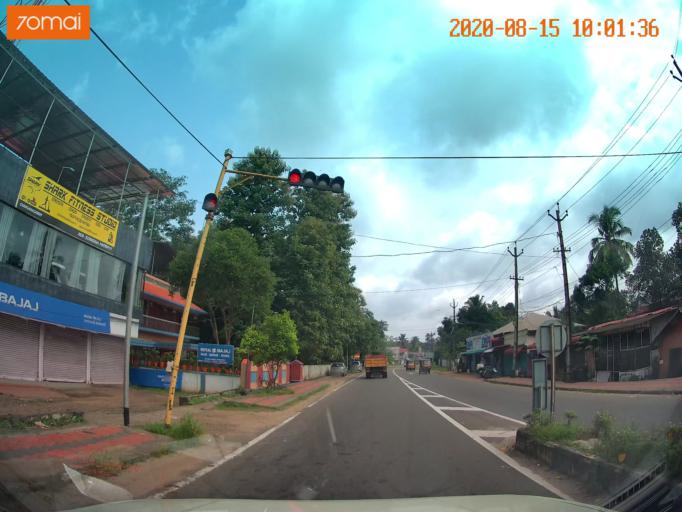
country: IN
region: Kerala
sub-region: Kottayam
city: Changanacheri
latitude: 9.4301
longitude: 76.5442
